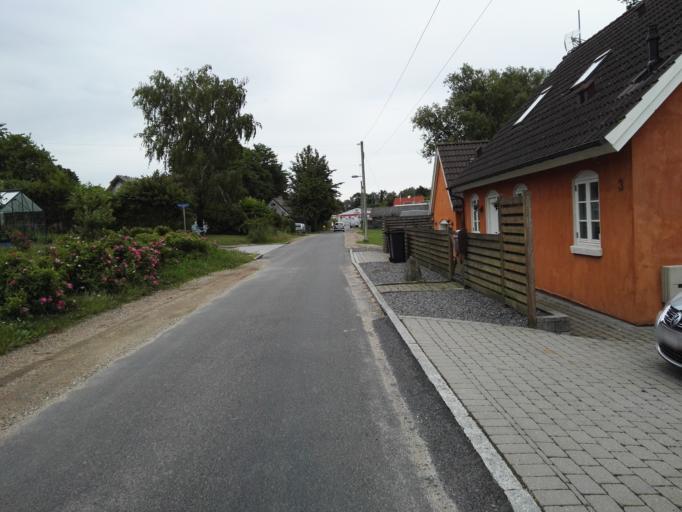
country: DK
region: Zealand
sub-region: Roskilde Kommune
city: Jyllinge
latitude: 55.7971
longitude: 12.1127
